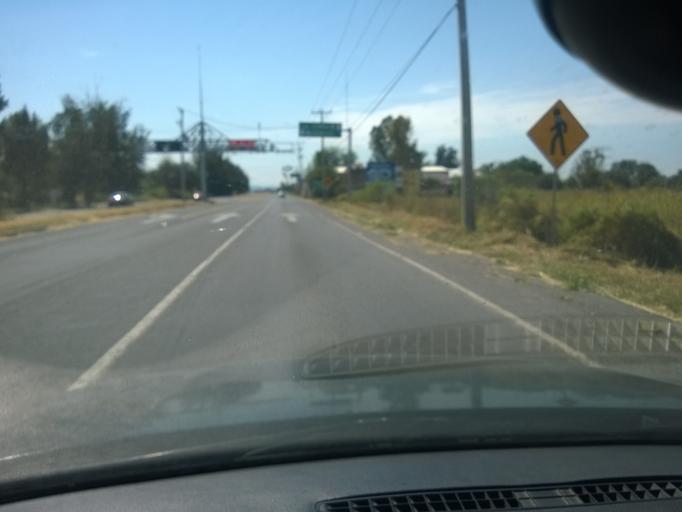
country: MX
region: Guanajuato
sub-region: Leon
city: El CERESO
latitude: 21.0256
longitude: -101.6970
